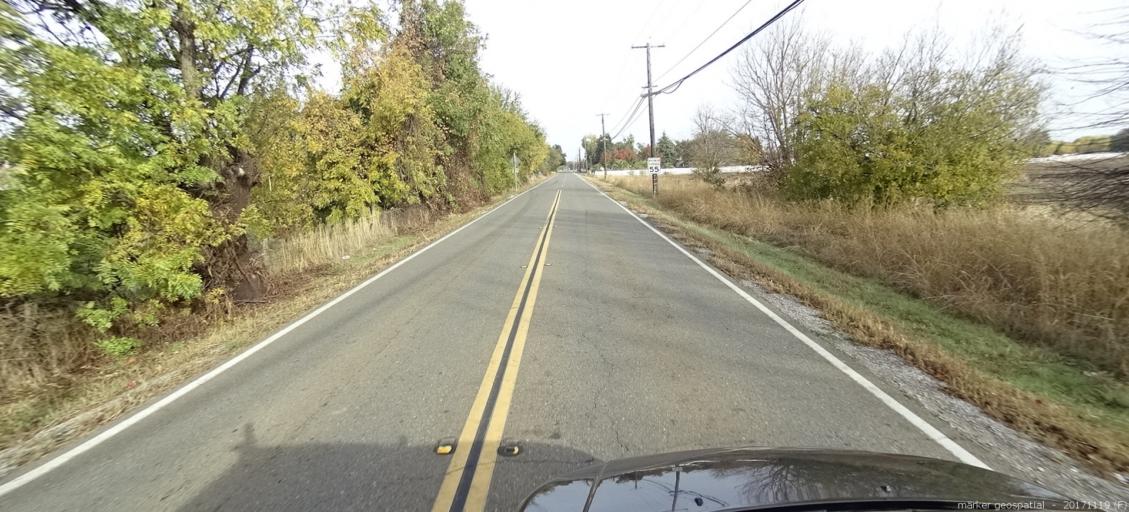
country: US
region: California
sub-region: Shasta County
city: Anderson
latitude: 40.5069
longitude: -122.3336
